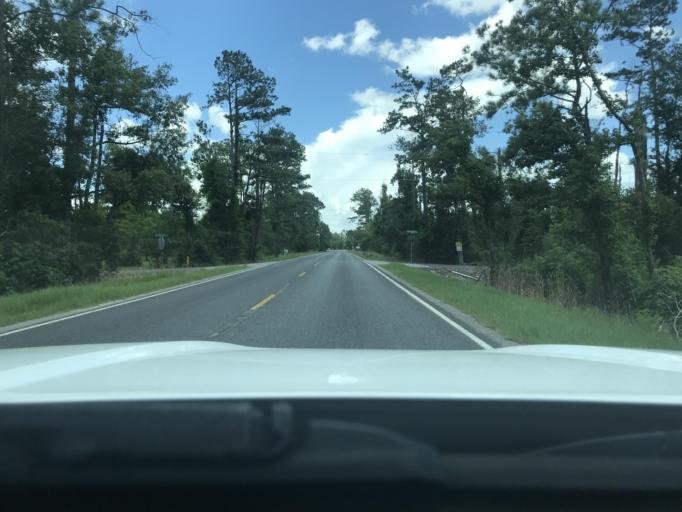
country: US
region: Louisiana
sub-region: Calcasieu Parish
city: Moss Bluff
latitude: 30.2771
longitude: -93.1750
